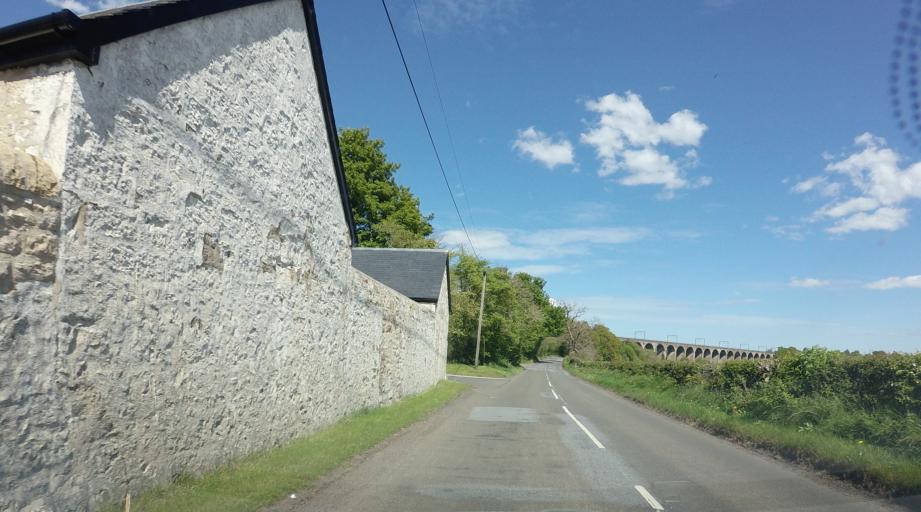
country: GB
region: Scotland
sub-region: West Lothian
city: Linlithgow
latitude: 55.9729
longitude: -3.6420
